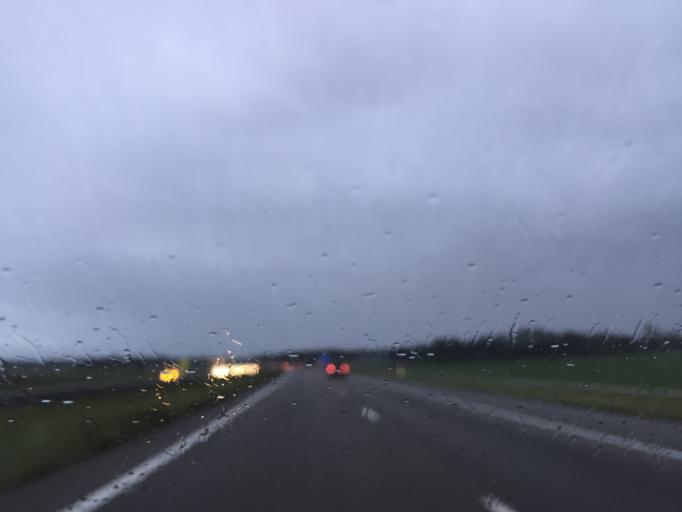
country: NL
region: North Brabant
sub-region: Gemeente Woensdrecht
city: Woensdrecht
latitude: 51.4362
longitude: 4.2988
